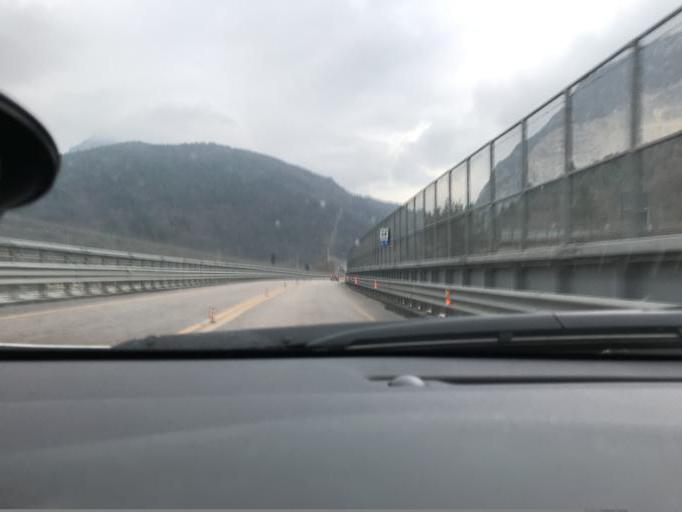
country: IT
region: The Marches
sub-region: Provincia di Ancona
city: Serra San Quirico
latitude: 43.4353
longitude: 13.0196
